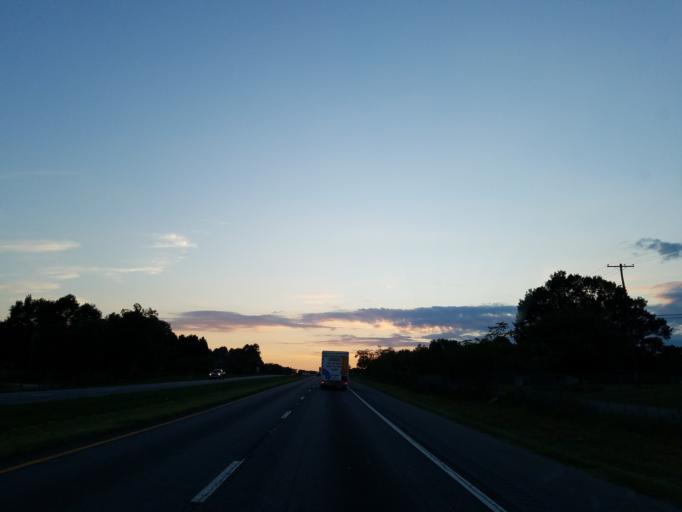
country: US
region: South Carolina
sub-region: Spartanburg County
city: Cowpens
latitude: 35.0739
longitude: -81.7506
